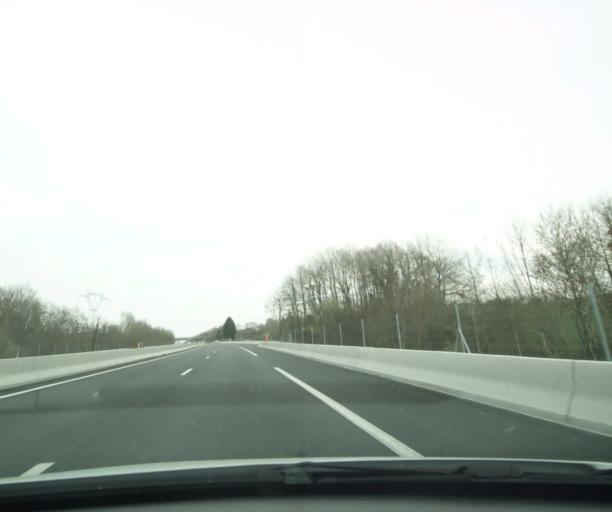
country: FR
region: Aquitaine
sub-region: Departement des Pyrenees-Atlantiques
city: Lahonce
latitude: 43.4480
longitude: -1.3752
